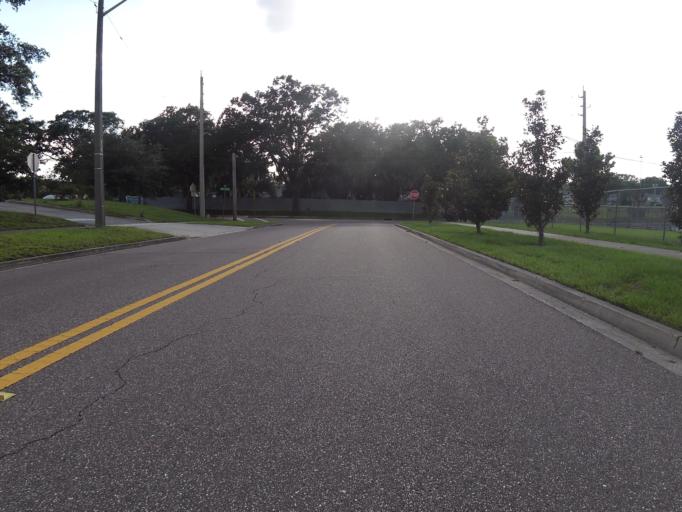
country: US
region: Florida
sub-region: Duval County
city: Jacksonville
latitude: 30.3399
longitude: -81.6625
